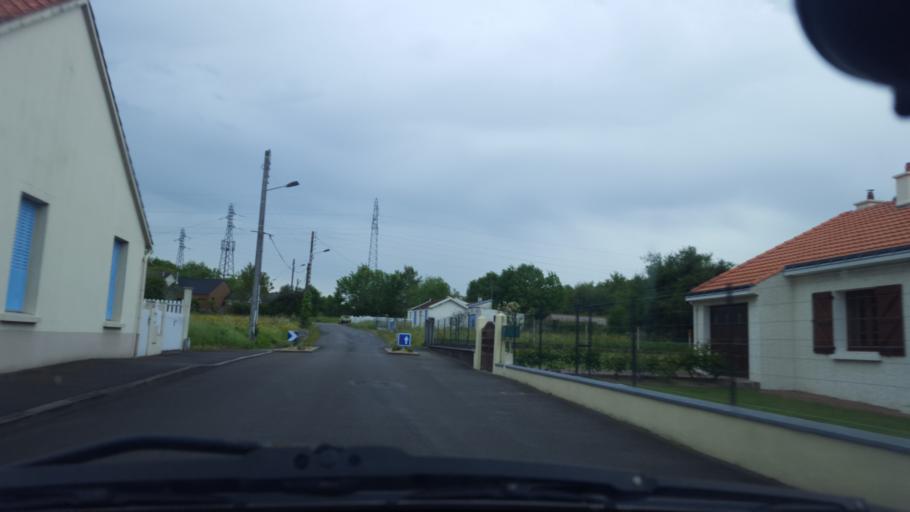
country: FR
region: Pays de la Loire
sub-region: Departement de la Loire-Atlantique
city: Les Sorinieres
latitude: 47.1680
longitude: -1.5260
